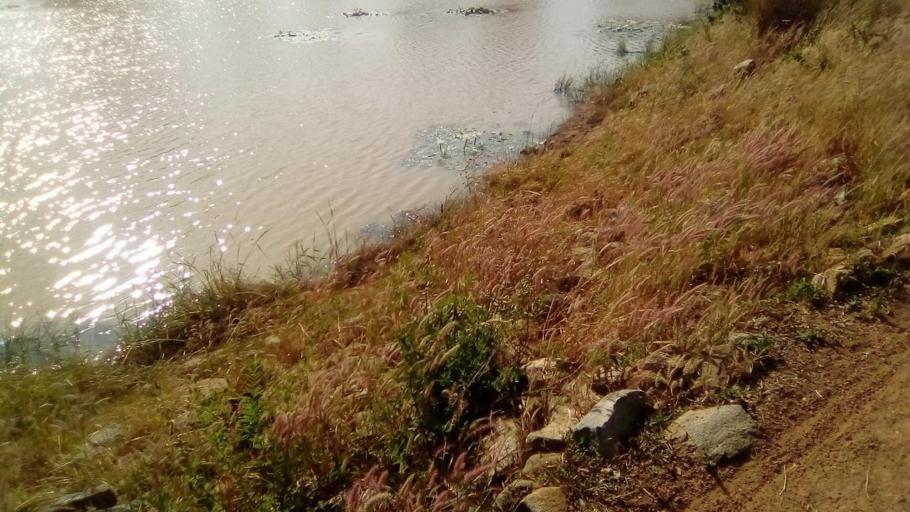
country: TG
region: Savanes
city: Dapaong
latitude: 11.0566
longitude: 0.1236
